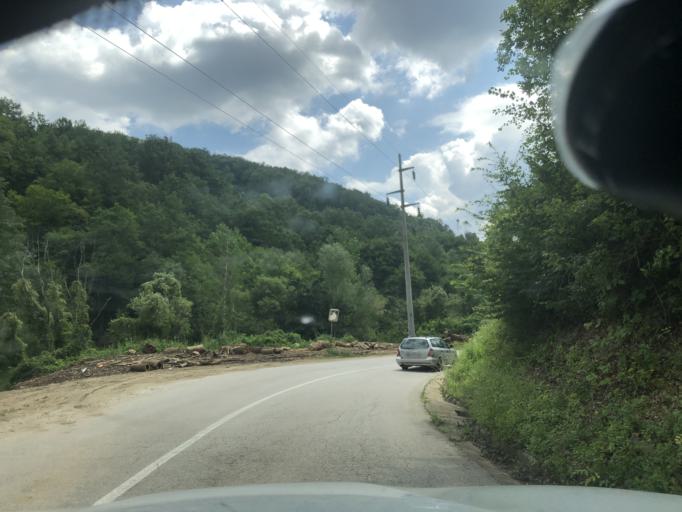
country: RS
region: Central Serbia
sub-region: Jablanicki Okrug
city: Medvega
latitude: 42.7913
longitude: 21.5825
